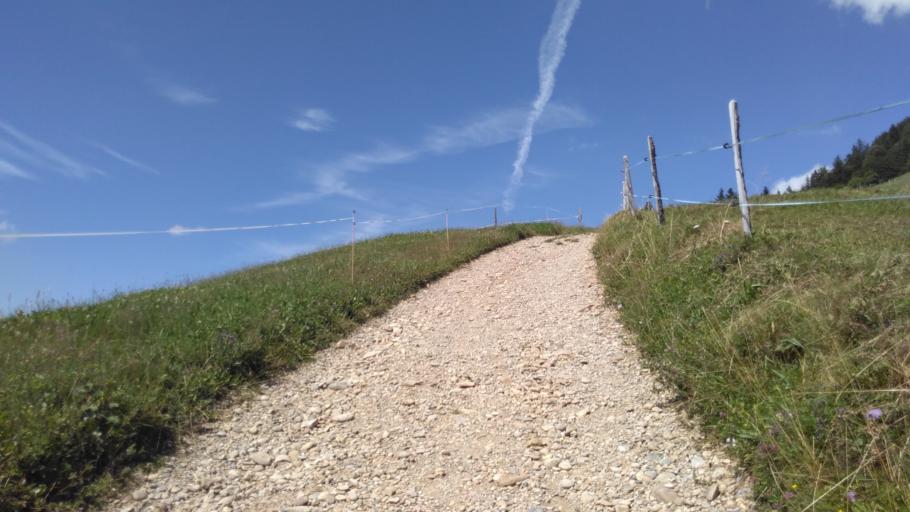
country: CH
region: Saint Gallen
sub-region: Wahlkreis See-Gaster
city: Goldingen
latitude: 47.2944
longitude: 9.0004
